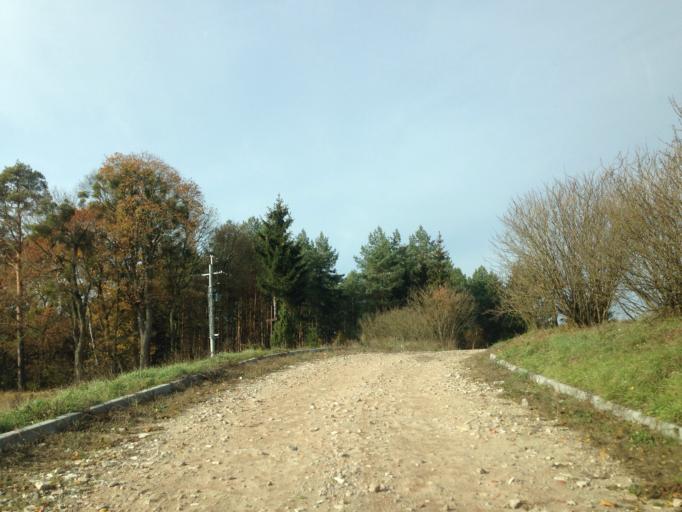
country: PL
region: Kujawsko-Pomorskie
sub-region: Powiat brodnicki
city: Gorzno
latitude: 53.2251
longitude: 19.6557
